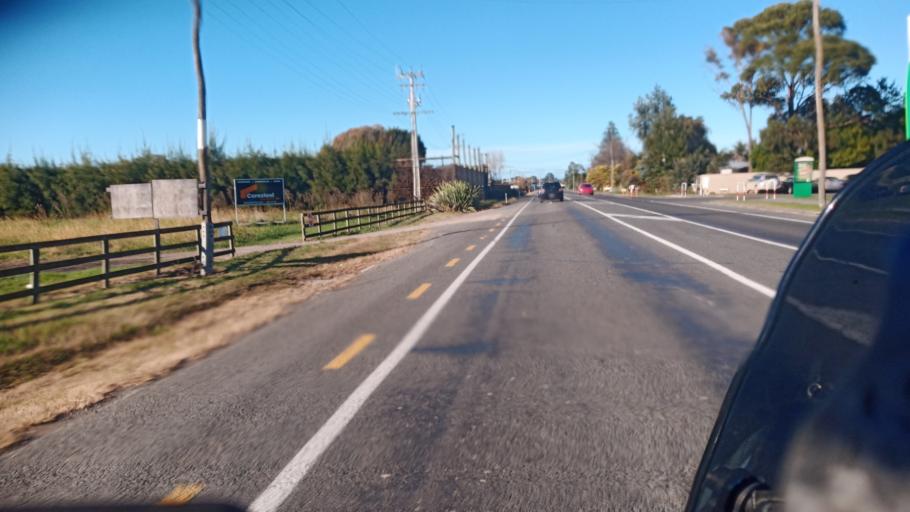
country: NZ
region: Hawke's Bay
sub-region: Napier City
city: Napier
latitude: -39.4250
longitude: 176.8698
